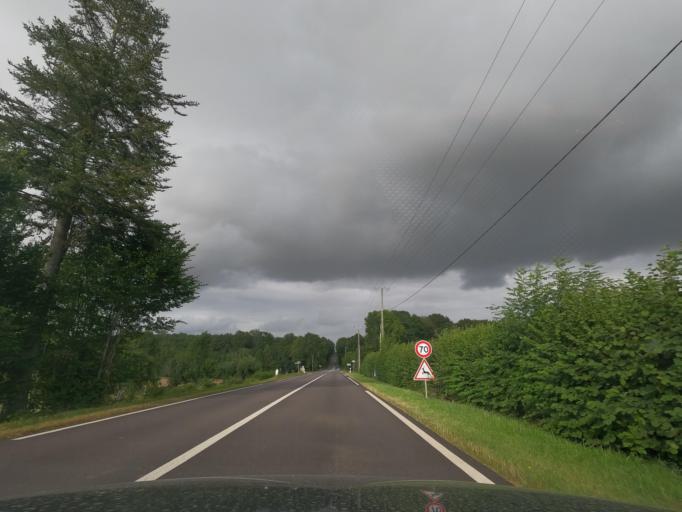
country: FR
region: Haute-Normandie
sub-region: Departement de l'Eure
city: Menneval
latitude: 49.1201
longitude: 0.6282
